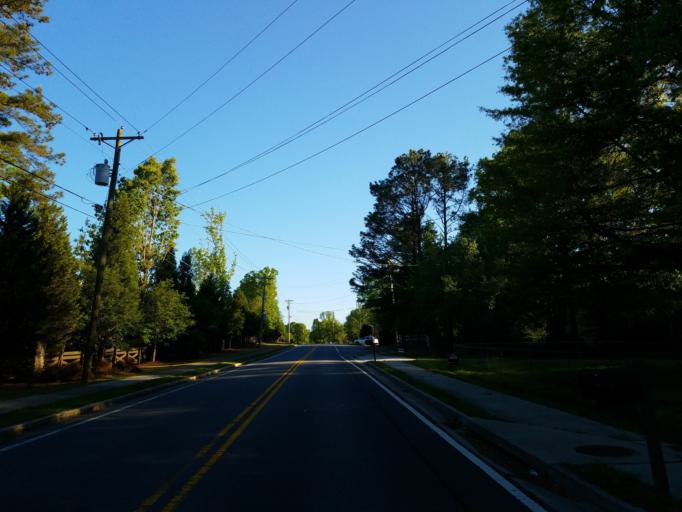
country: US
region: Georgia
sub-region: Cobb County
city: Powder Springs
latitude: 33.9344
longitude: -84.6409
